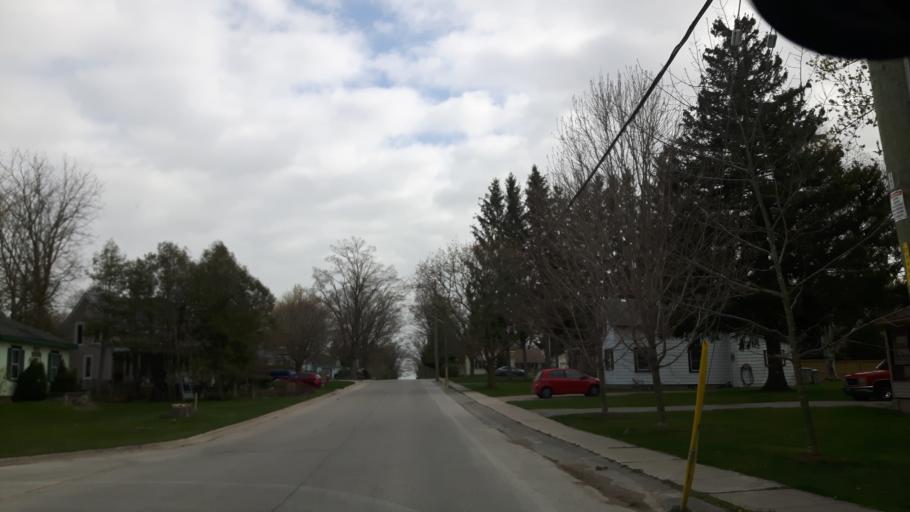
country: CA
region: Ontario
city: Bluewater
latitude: 43.6176
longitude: -81.5451
